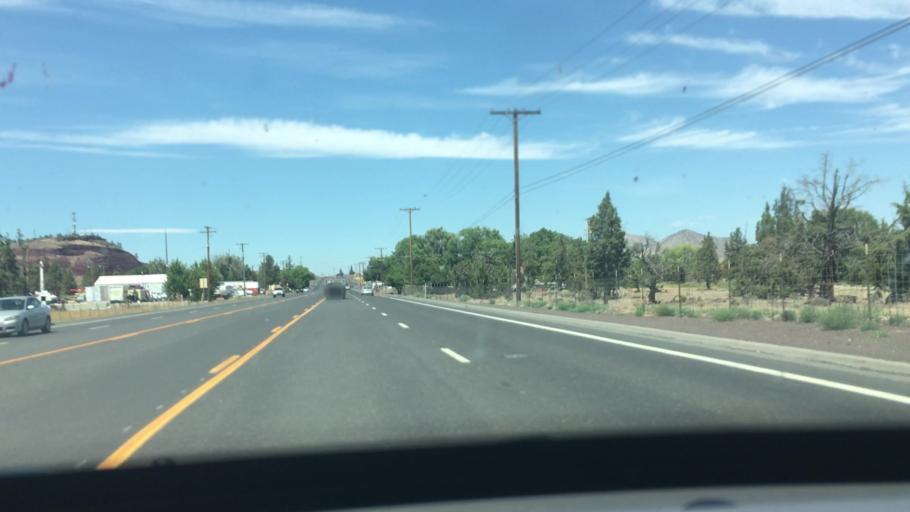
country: US
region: Oregon
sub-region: Deschutes County
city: Redmond
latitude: 44.3079
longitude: -121.1724
